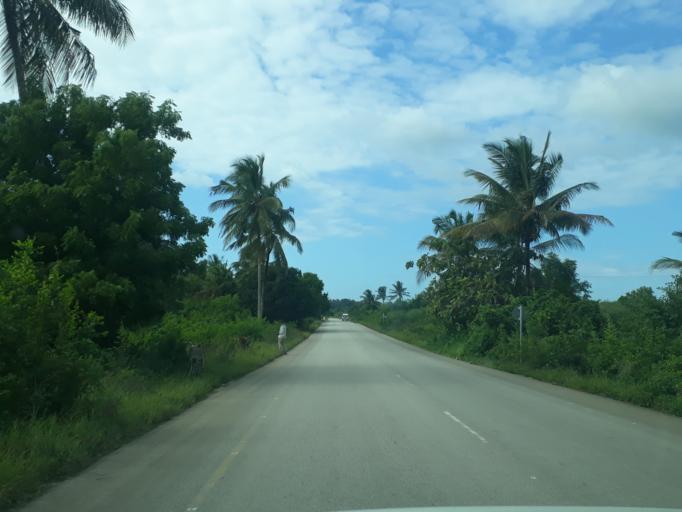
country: TZ
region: Zanzibar North
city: Kijini
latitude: -5.8398
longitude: 39.2850
